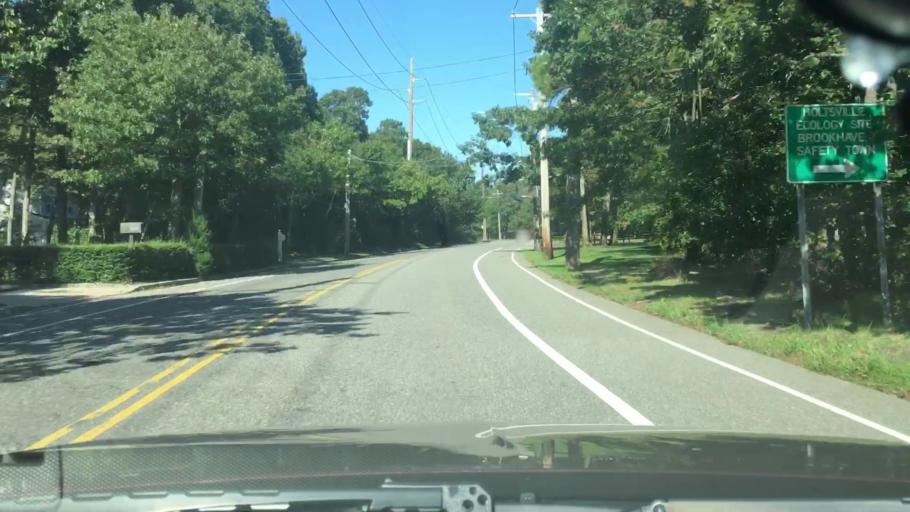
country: US
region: New York
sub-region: Suffolk County
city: Holtsville
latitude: 40.7974
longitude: -73.0382
